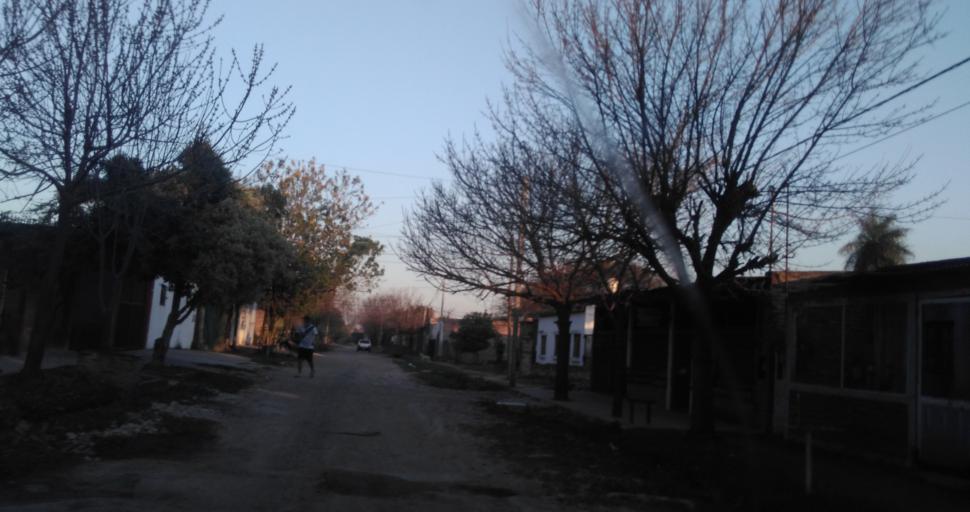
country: AR
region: Chaco
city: Fontana
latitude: -27.4268
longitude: -59.0019
